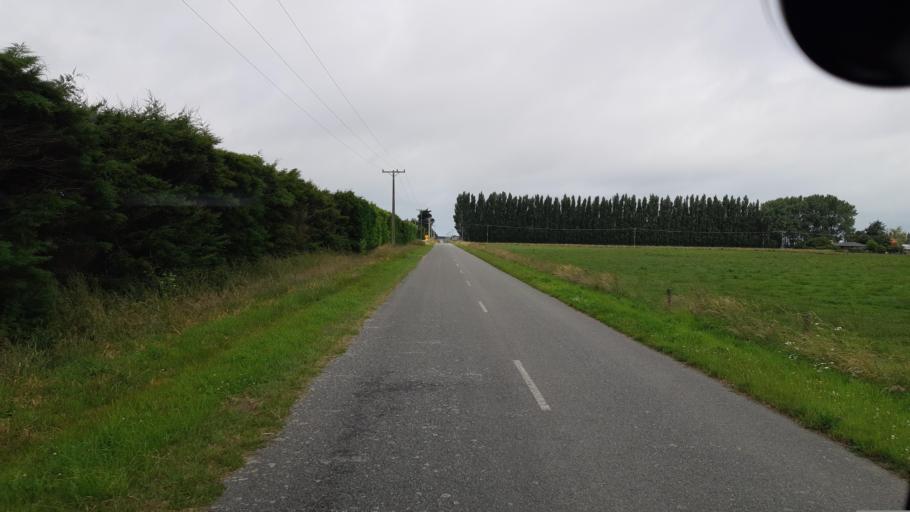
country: NZ
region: Canterbury
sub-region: Timaru District
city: Timaru
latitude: -44.2516
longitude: 171.3637
